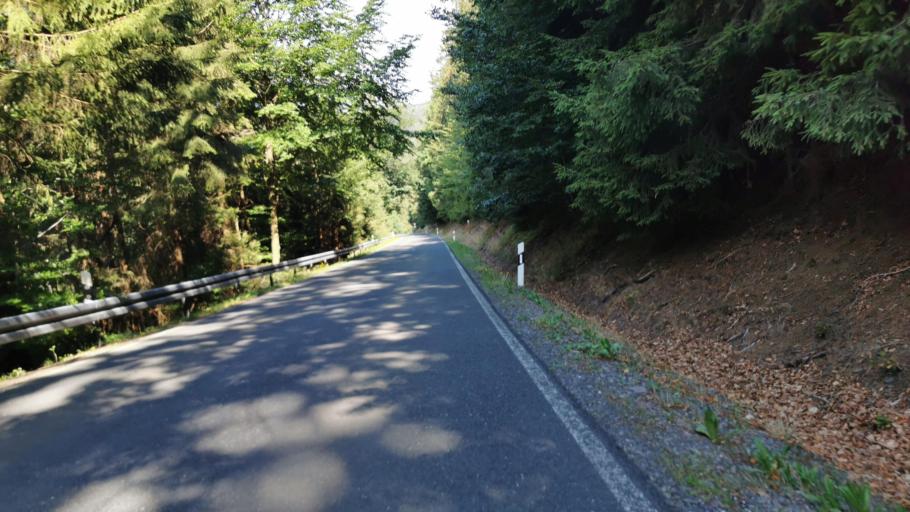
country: DE
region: Bavaria
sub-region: Upper Franconia
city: Tettau
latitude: 50.4361
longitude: 11.2690
